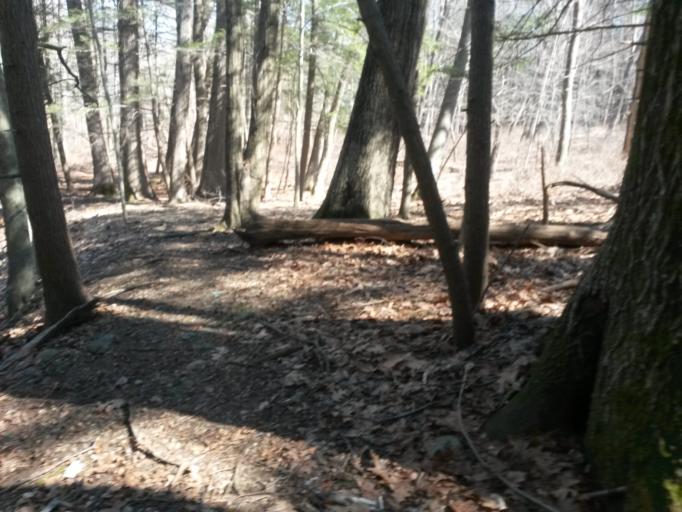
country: US
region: New York
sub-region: Westchester County
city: Yorktown Heights
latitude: 41.2804
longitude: -73.7511
